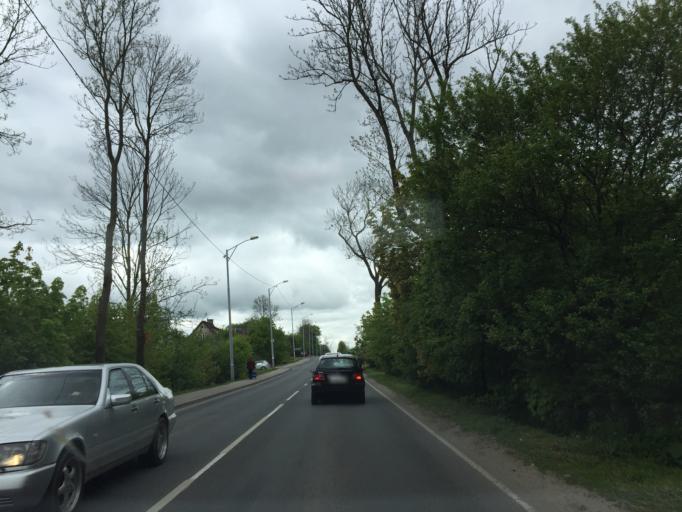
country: RU
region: Kaliningrad
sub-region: Gorod Kaliningrad
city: Kaliningrad
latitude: 54.6735
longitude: 20.4372
